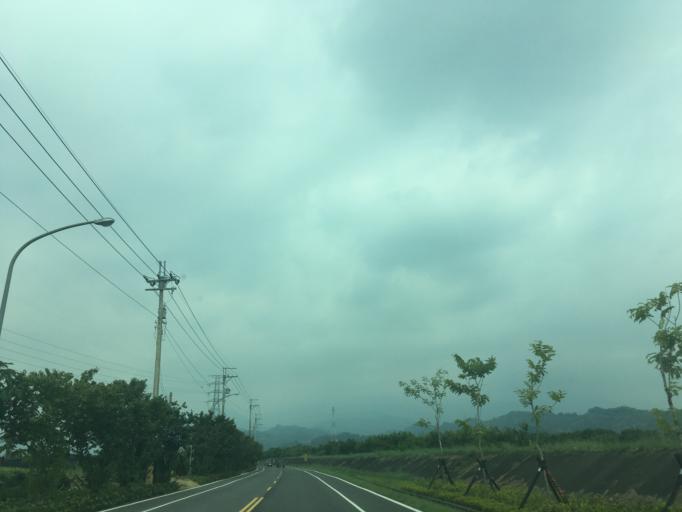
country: TW
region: Taiwan
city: Fengyuan
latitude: 24.2909
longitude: 120.8421
